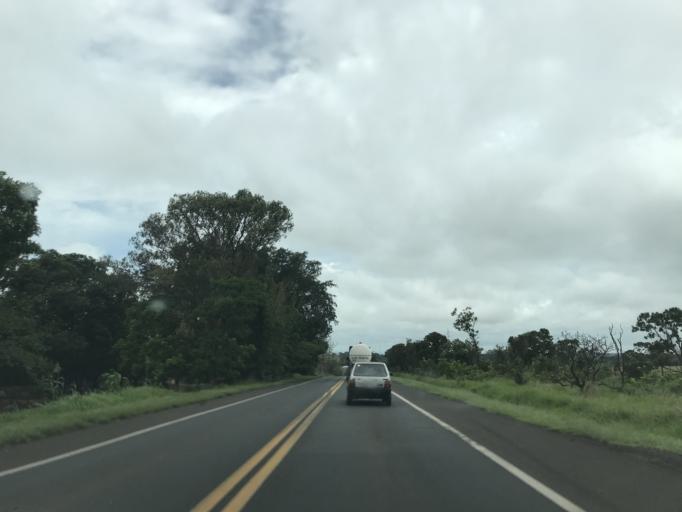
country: BR
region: Minas Gerais
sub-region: Frutal
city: Frutal
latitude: -19.8057
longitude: -48.9676
